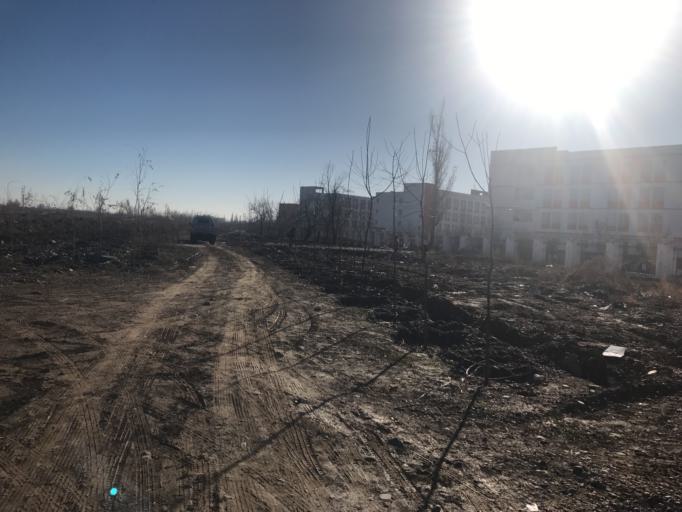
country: CN
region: Xinjiang Uygur Zizhiqu
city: Yili
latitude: 43.9366
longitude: 81.3653
